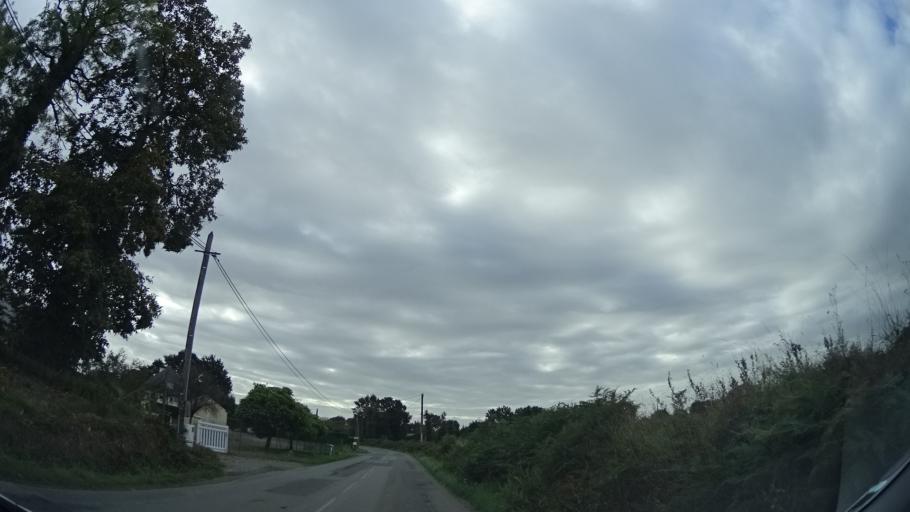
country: FR
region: Brittany
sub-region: Departement d'Ille-et-Vilaine
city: Dinge
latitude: 48.3566
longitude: -1.7093
